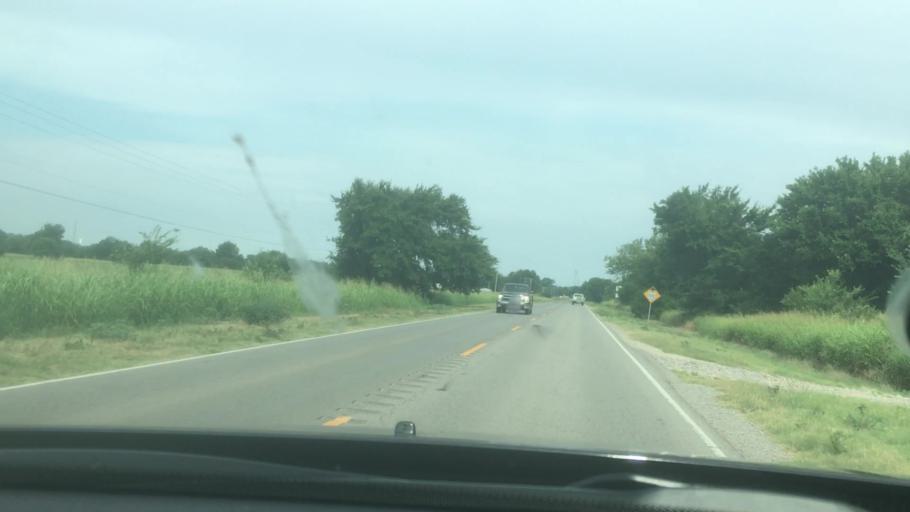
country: US
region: Oklahoma
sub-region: Garvin County
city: Maysville
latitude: 34.8144
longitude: -97.3898
